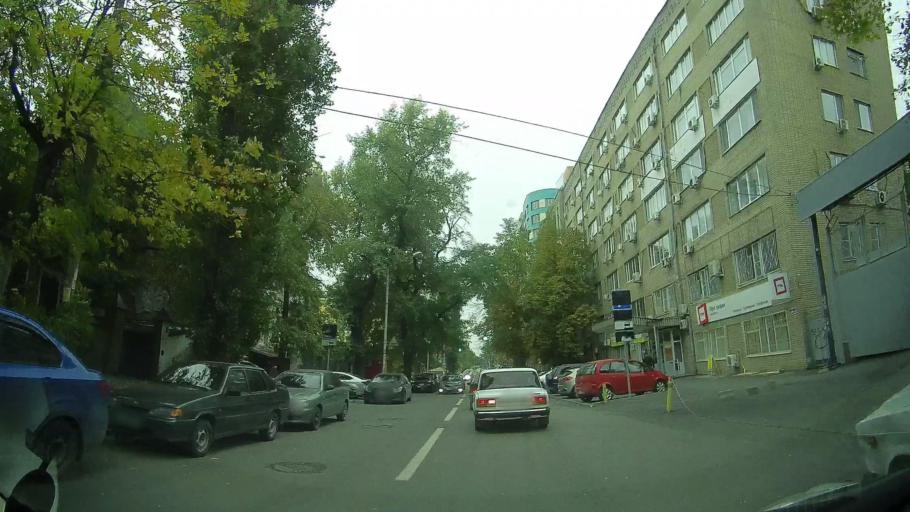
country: RU
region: Rostov
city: Rostov-na-Donu
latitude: 47.2290
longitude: 39.7218
